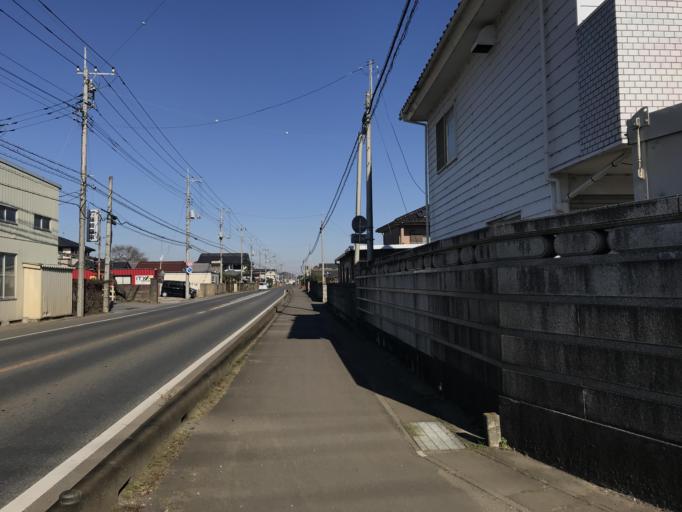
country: JP
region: Tochigi
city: Oyama
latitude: 36.2547
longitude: 139.8373
